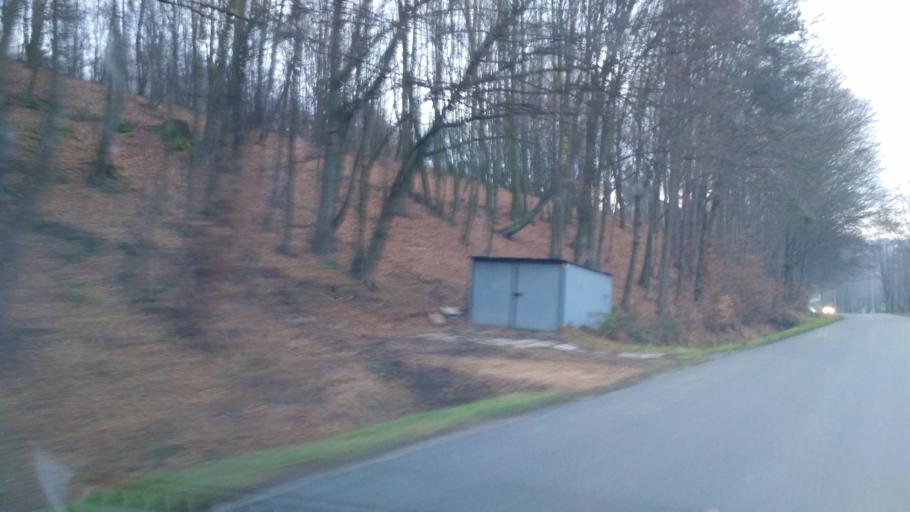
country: PL
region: Subcarpathian Voivodeship
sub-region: Powiat strzyzowski
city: Niebylec
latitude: 49.8637
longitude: 21.8896
